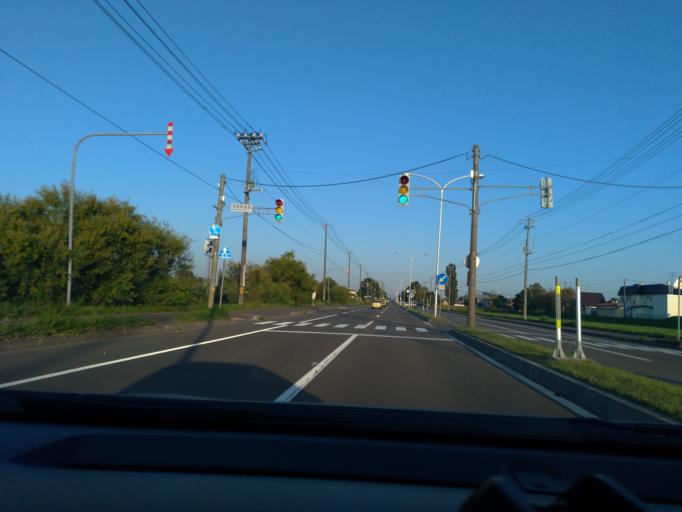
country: JP
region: Hokkaido
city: Ishikari
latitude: 43.1606
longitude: 141.3700
